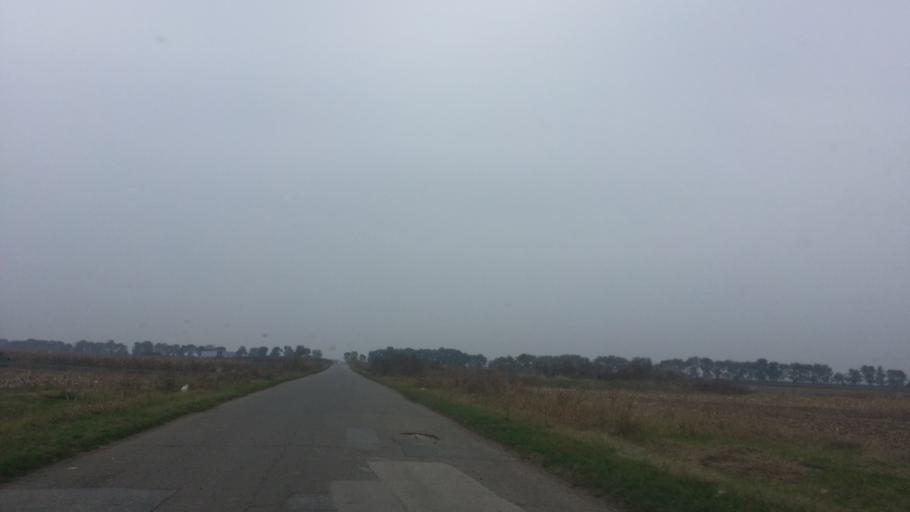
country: RS
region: Autonomna Pokrajina Vojvodina
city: Nova Pazova
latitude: 44.9575
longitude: 20.2183
